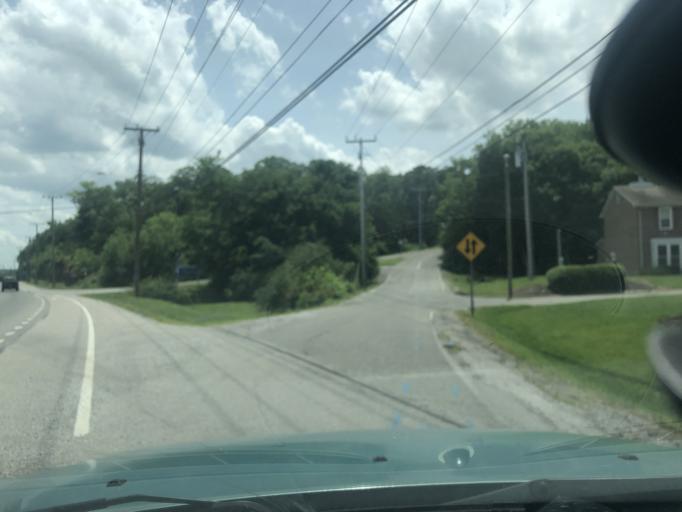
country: US
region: Tennessee
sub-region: Davidson County
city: Lakewood
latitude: 36.1251
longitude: -86.6302
